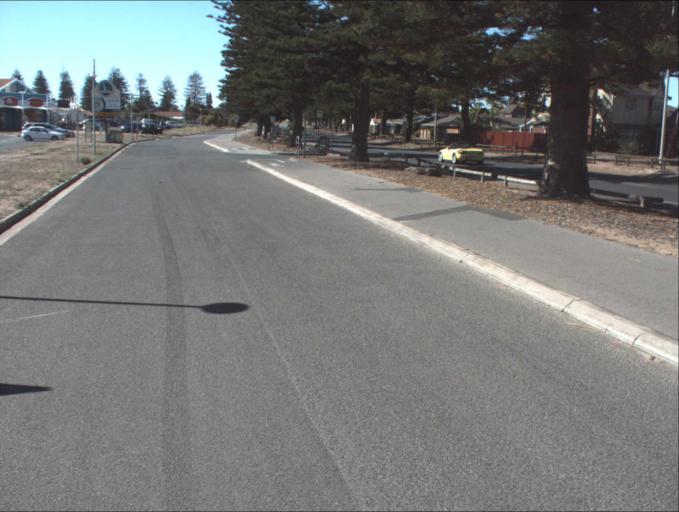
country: AU
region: South Australia
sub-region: Port Adelaide Enfield
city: Birkenhead
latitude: -34.7868
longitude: 138.4896
